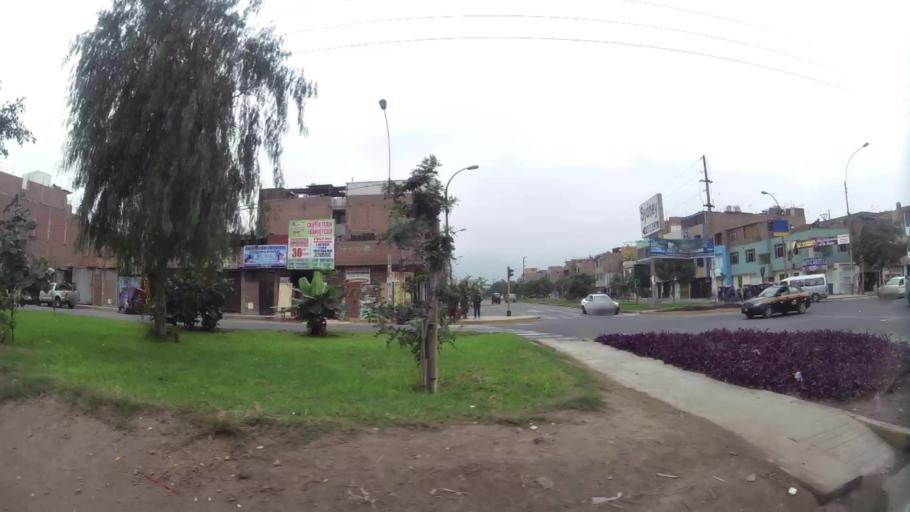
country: PE
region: Lima
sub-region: Lima
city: Independencia
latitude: -11.9543
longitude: -77.0761
